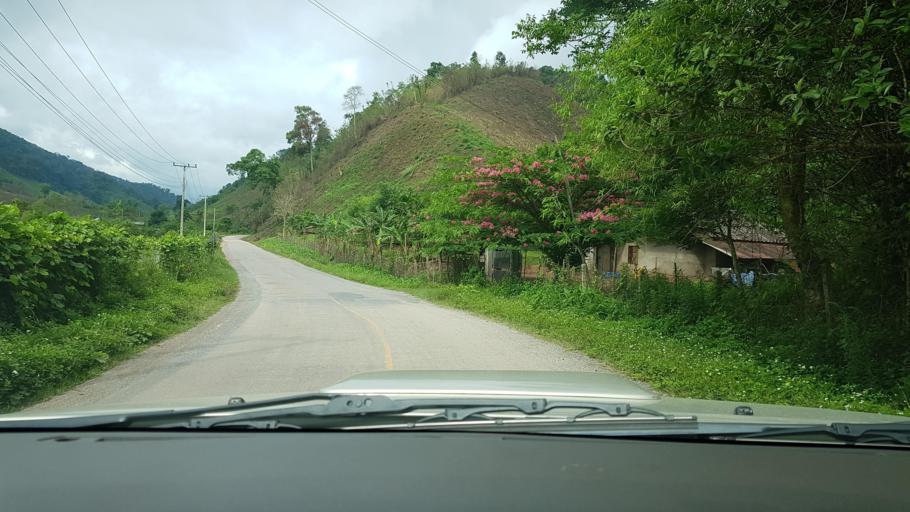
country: LA
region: Oudomxai
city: Muang Xay
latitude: 20.5633
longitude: 101.9166
